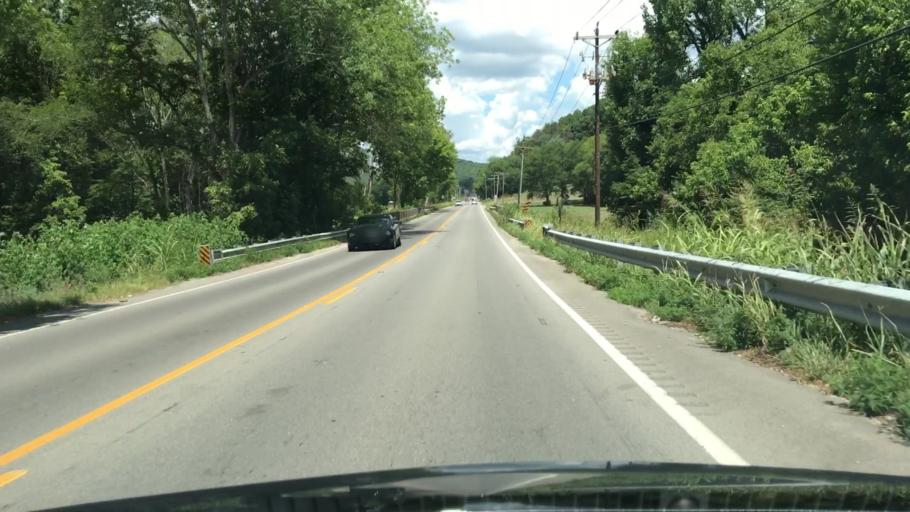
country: US
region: Tennessee
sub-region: Williamson County
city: Nolensville
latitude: 35.8833
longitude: -86.6625
